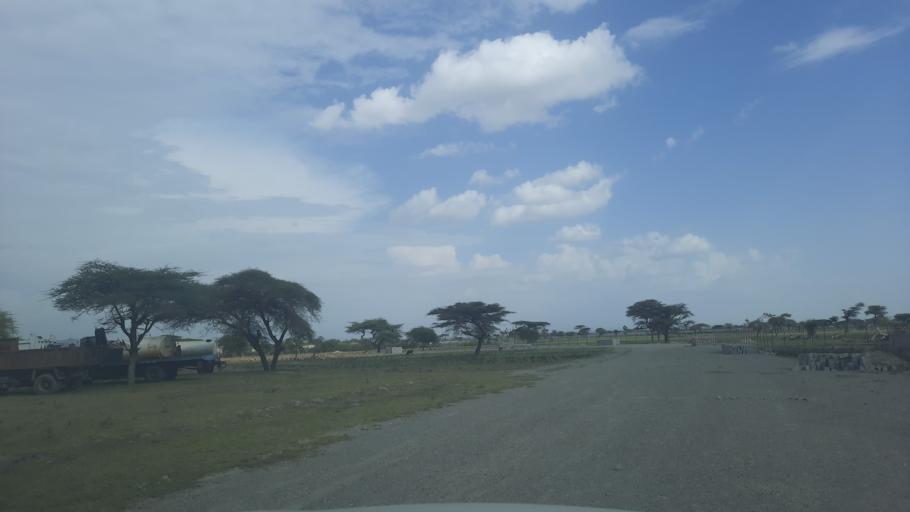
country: ET
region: Oromiya
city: Ziway
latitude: 7.6986
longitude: 38.6556
